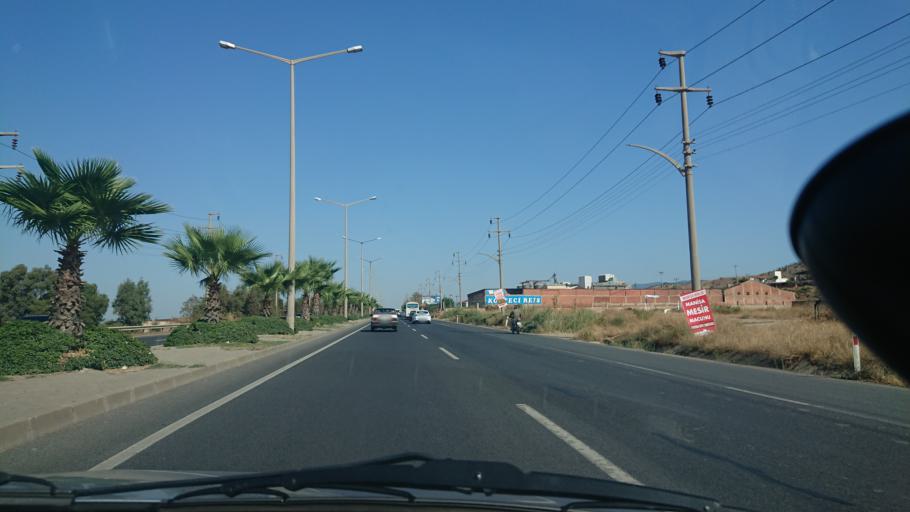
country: TR
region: Manisa
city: Turgutlu
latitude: 38.4957
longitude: 27.7393
